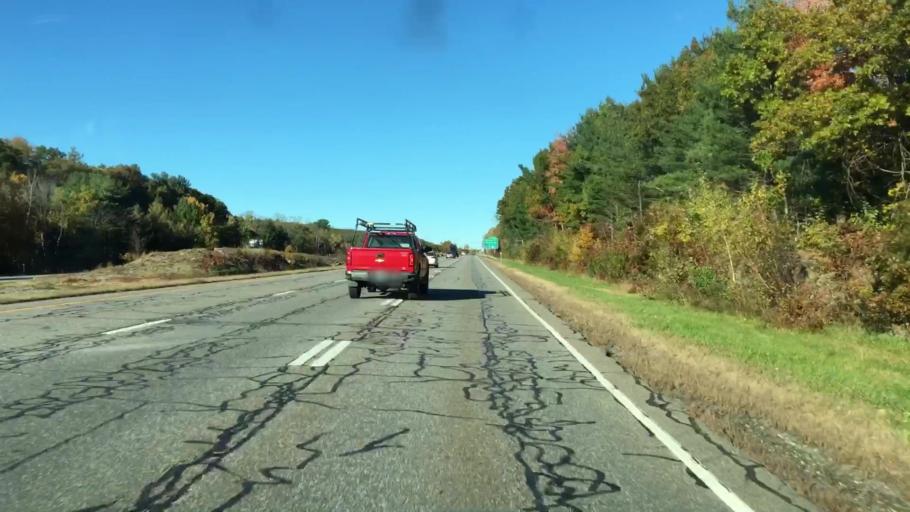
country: US
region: Connecticut
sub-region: Litchfield County
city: Torrington
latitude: 41.8185
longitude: -73.1124
